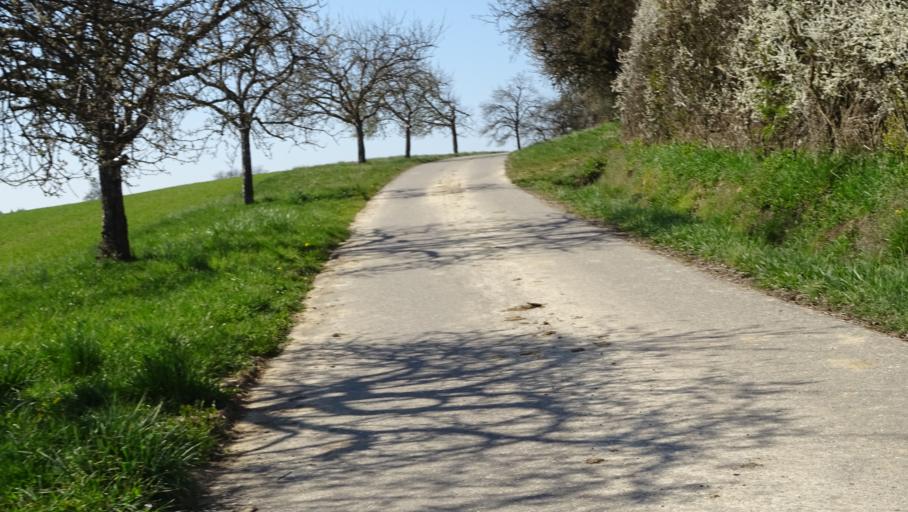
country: DE
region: Baden-Wuerttemberg
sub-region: Karlsruhe Region
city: Limbach
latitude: 49.4191
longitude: 9.2413
